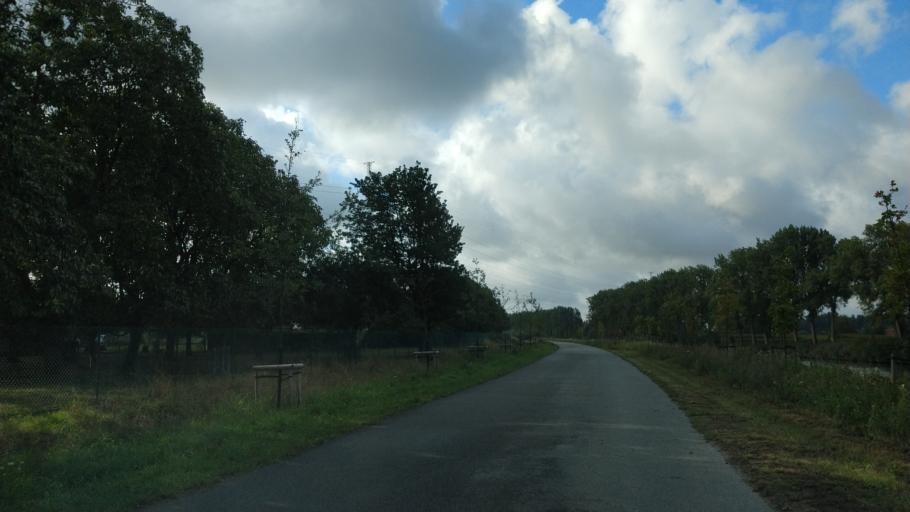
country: BE
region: Flanders
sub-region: Provincie Oost-Vlaanderen
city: Zomergem
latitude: 51.0885
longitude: 3.5634
